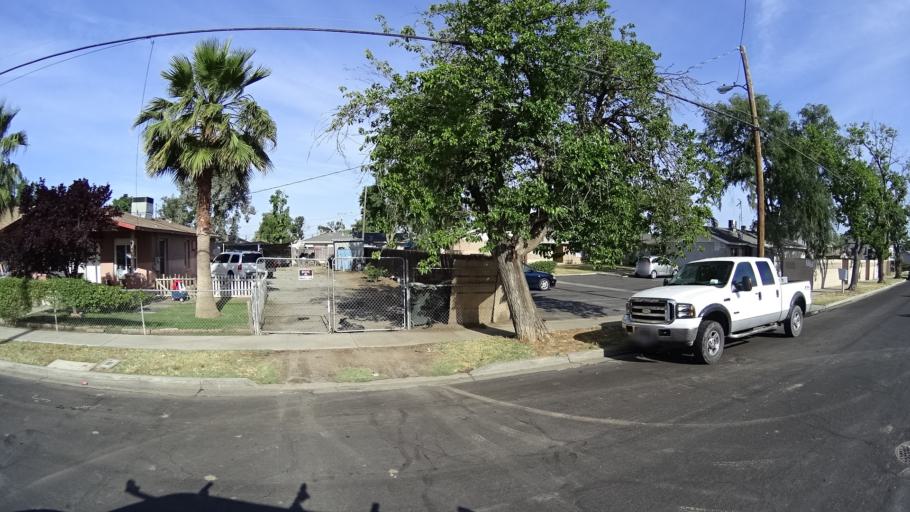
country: US
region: California
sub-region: Kings County
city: Hanford
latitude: 36.3189
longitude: -119.6460
